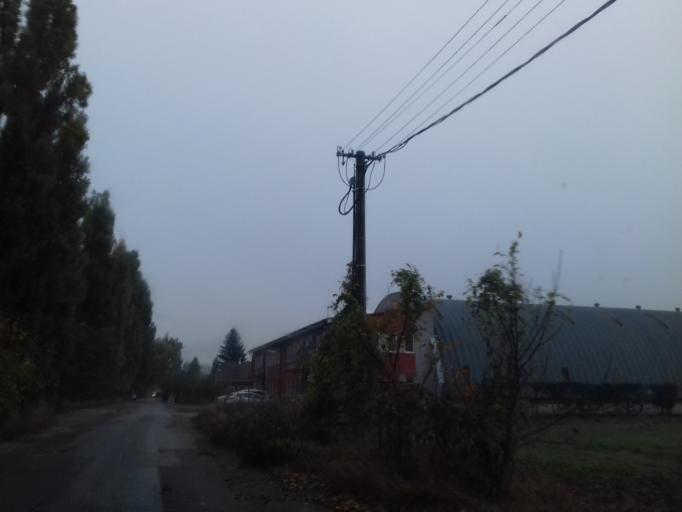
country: SK
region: Bratislavsky
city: Bratislava
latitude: 48.1372
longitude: 17.1717
